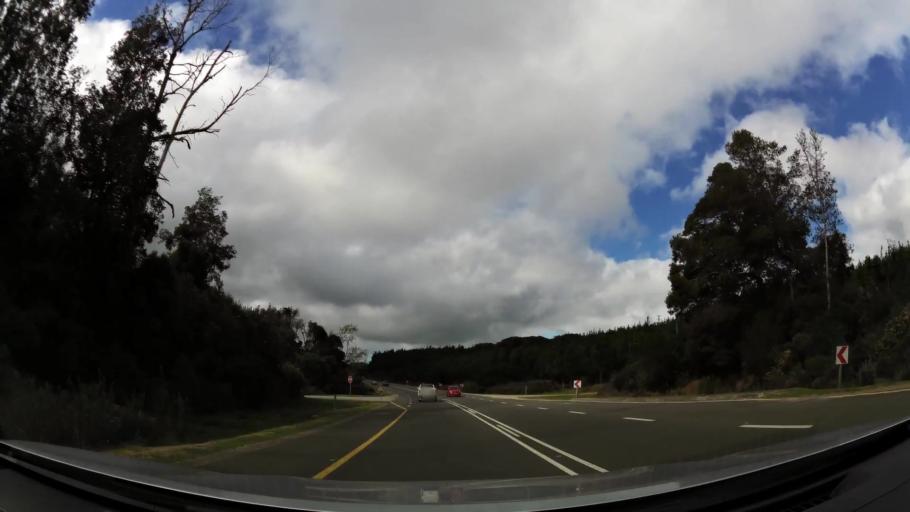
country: ZA
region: Western Cape
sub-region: Eden District Municipality
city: Knysna
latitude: -34.0288
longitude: 23.1807
